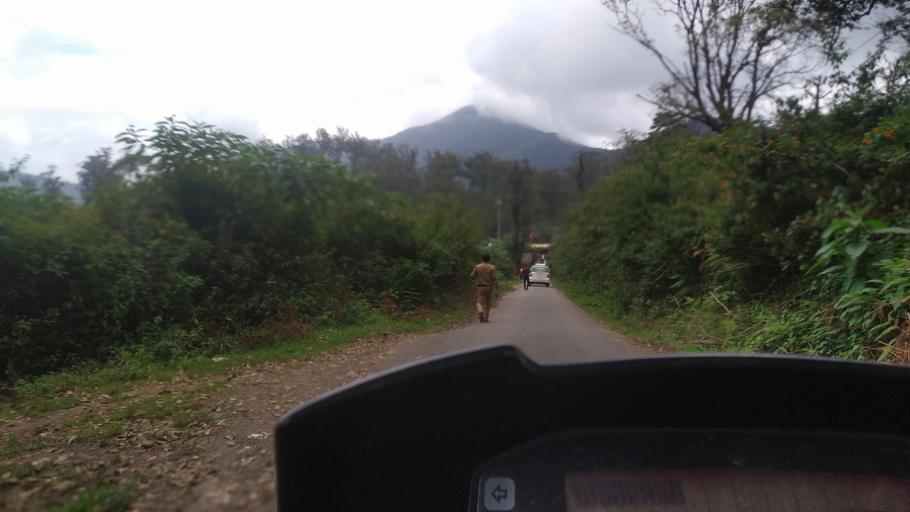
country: IN
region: Kerala
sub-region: Idukki
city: Munnar
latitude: 10.0666
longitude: 77.1076
